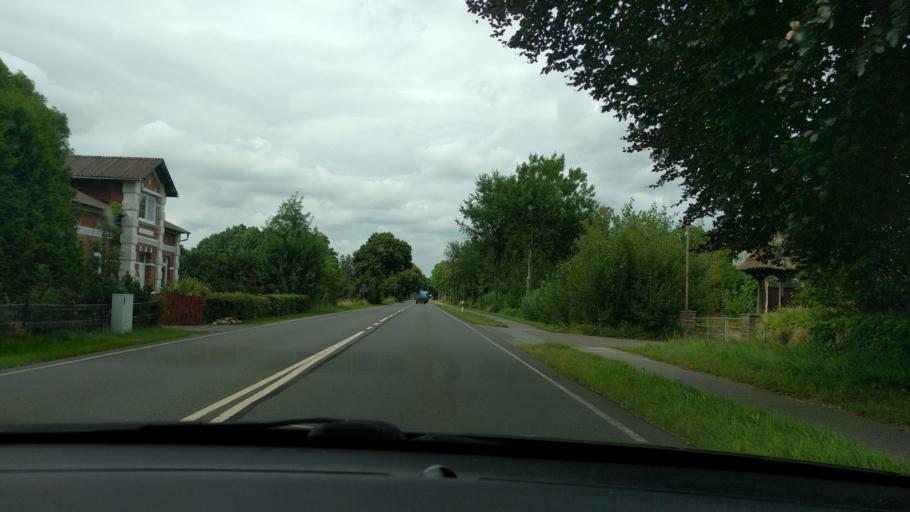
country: DE
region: Schleswig-Holstein
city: Weddingstedt
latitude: 54.2326
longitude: 9.0806
